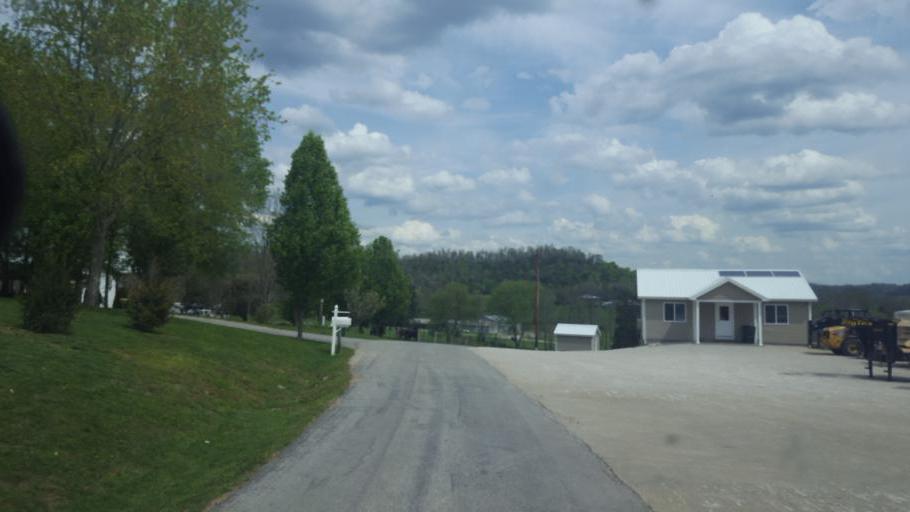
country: US
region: Kentucky
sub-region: Hart County
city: Munfordville
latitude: 37.2556
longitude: -85.9738
